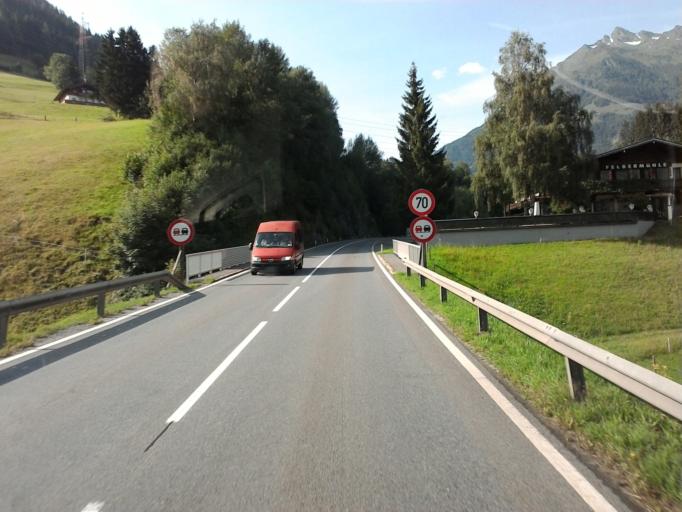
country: AT
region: Salzburg
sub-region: Politischer Bezirk Zell am See
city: Mittersill
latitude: 47.2743
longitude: 12.4879
